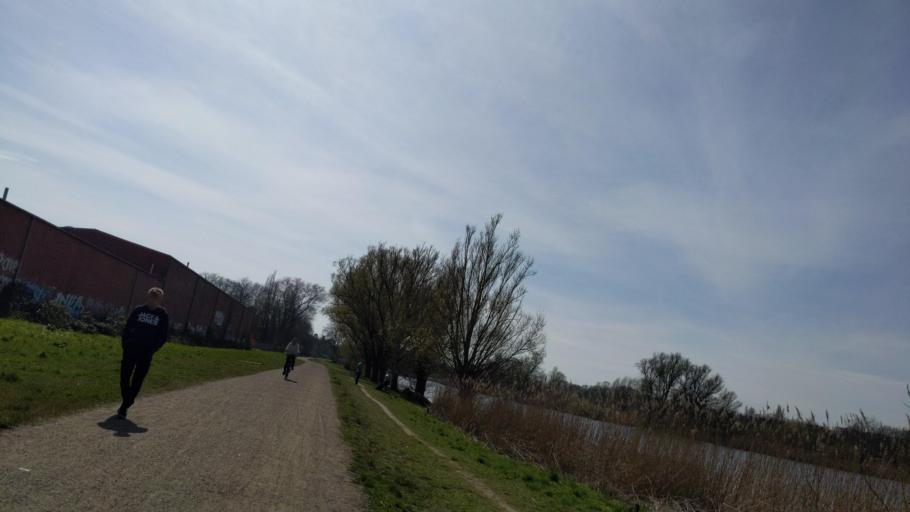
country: DE
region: Schleswig-Holstein
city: Luebeck
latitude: 53.8490
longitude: 10.6688
